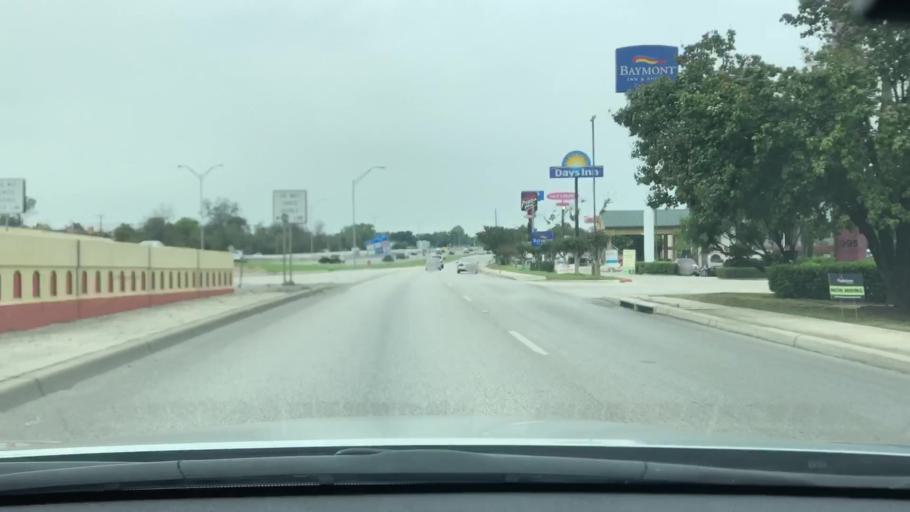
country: US
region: Texas
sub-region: Comal County
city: New Braunfels
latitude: 29.6983
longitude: -98.0968
